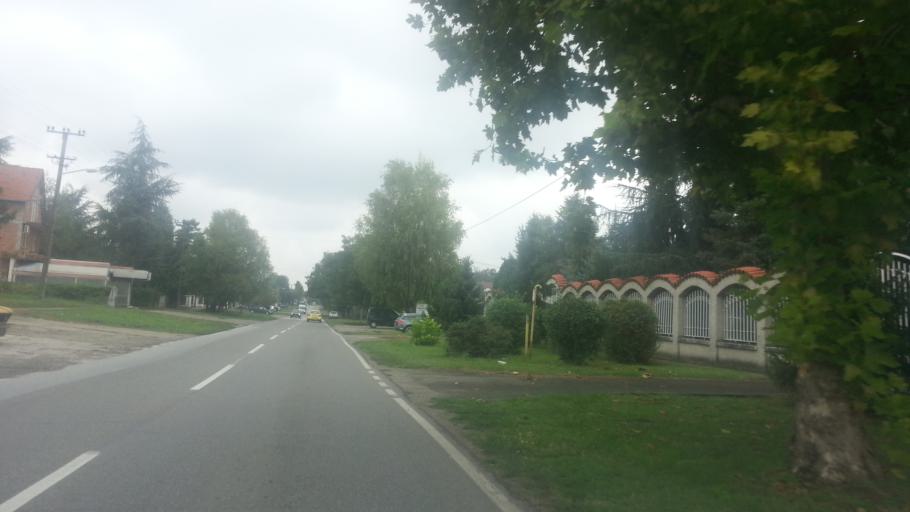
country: RS
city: Stari Banovci
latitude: 44.9702
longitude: 20.2816
